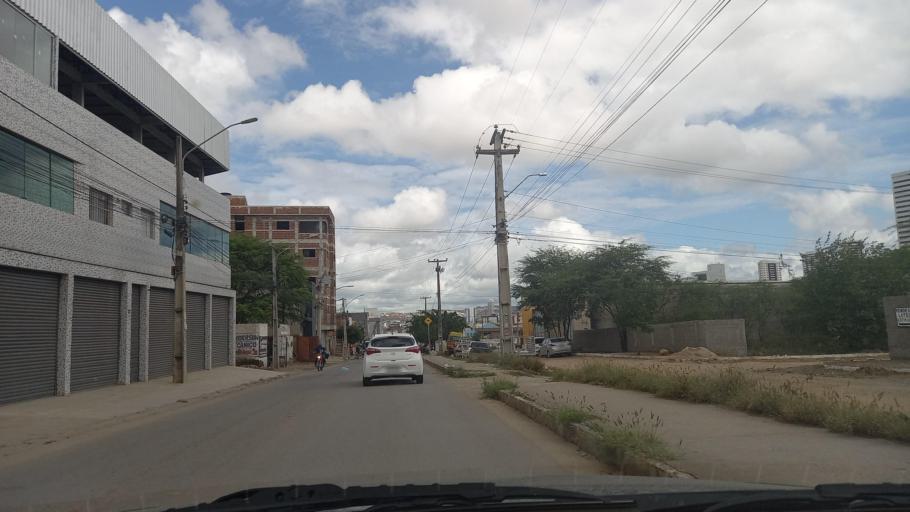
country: BR
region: Pernambuco
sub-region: Caruaru
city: Caruaru
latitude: -8.2639
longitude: -35.9602
